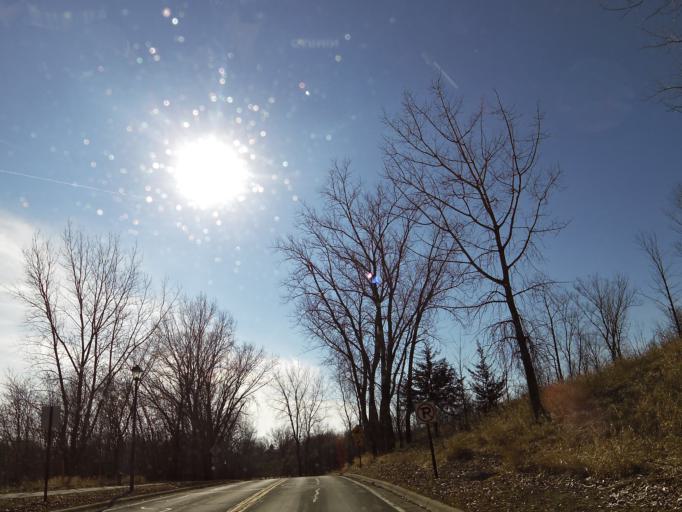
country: US
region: Minnesota
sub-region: Scott County
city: Prior Lake
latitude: 44.7087
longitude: -93.4617
